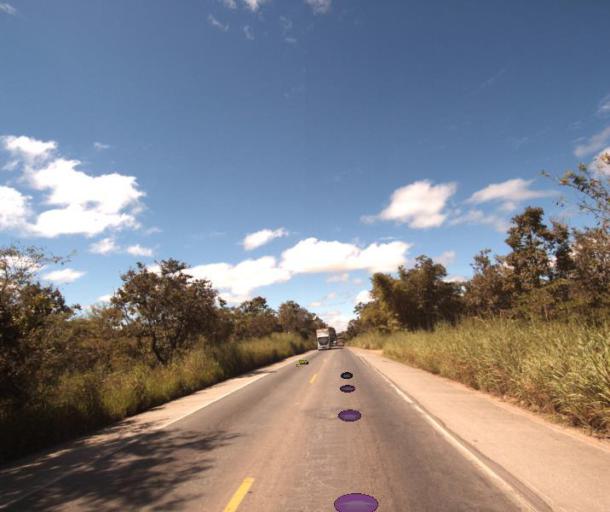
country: BR
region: Goias
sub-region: Rialma
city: Rialma
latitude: -15.4865
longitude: -49.4915
